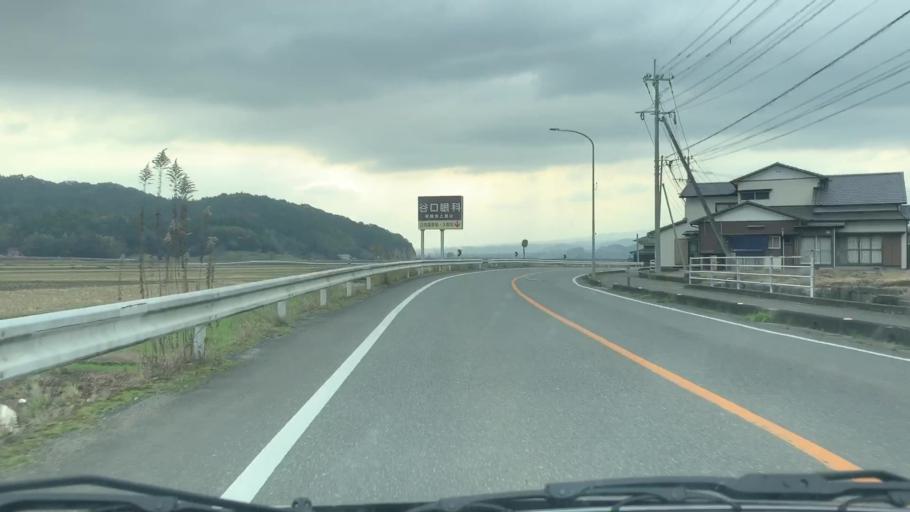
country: JP
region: Saga Prefecture
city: Kashima
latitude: 33.1443
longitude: 130.0638
